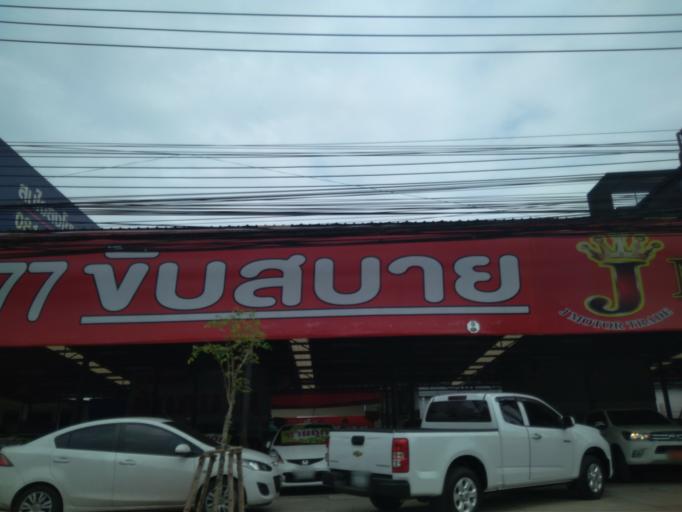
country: TH
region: Bangkok
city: Suan Luang
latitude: 13.7097
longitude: 100.6445
